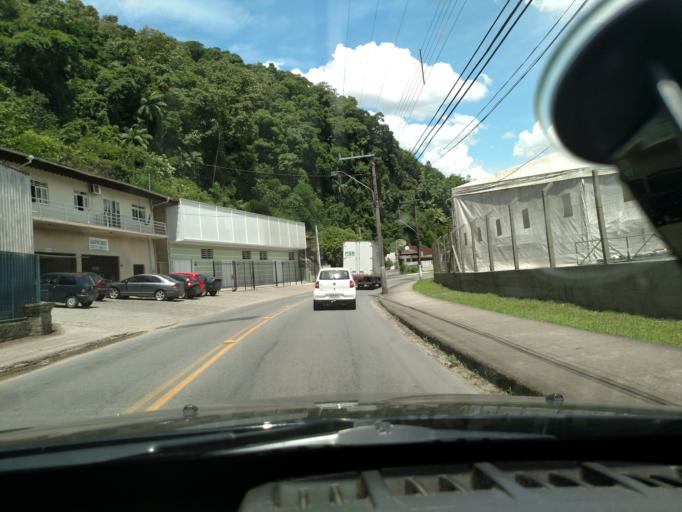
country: BR
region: Santa Catarina
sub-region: Blumenau
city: Blumenau
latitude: -26.9764
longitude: -49.0762
